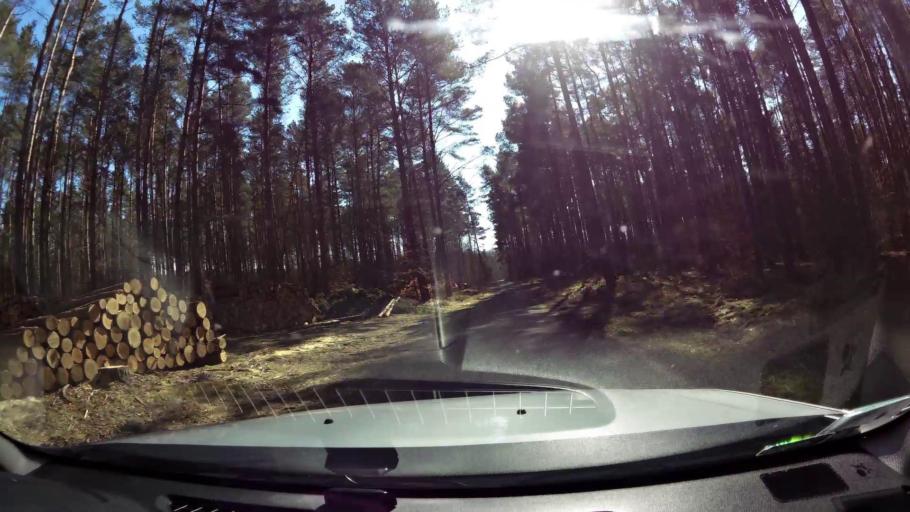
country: PL
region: West Pomeranian Voivodeship
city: Trzcinsko Zdroj
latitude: 53.0306
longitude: 14.6335
